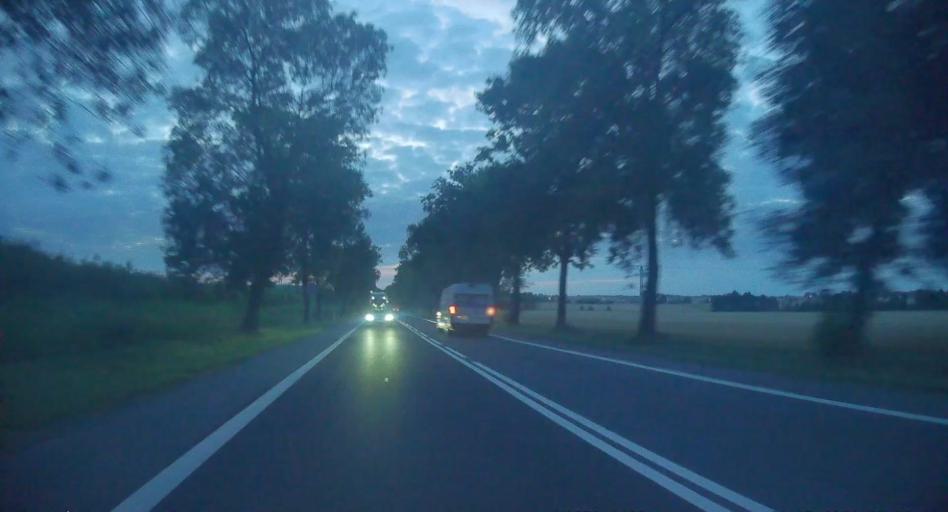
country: PL
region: Silesian Voivodeship
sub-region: Powiat klobucki
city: Klobuck
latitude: 50.9171
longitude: 18.8889
